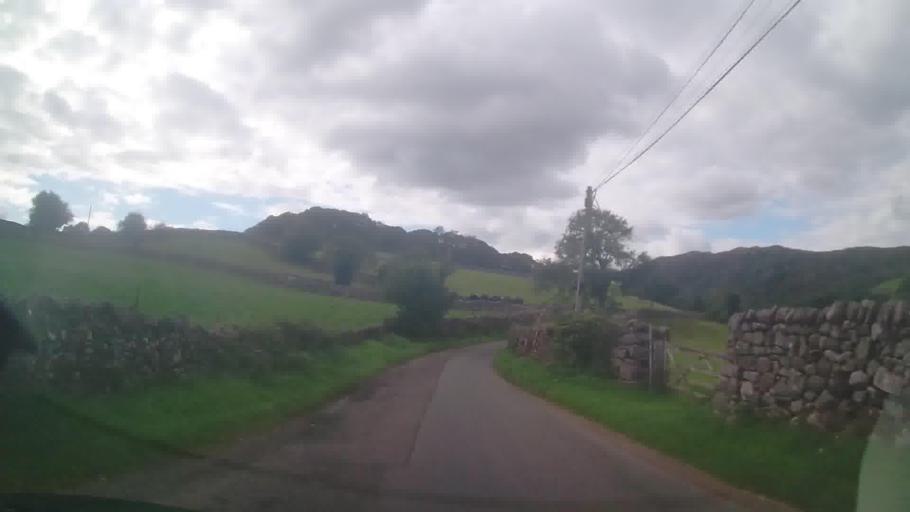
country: GB
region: England
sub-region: Cumbria
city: Millom
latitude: 54.3970
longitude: -3.2579
